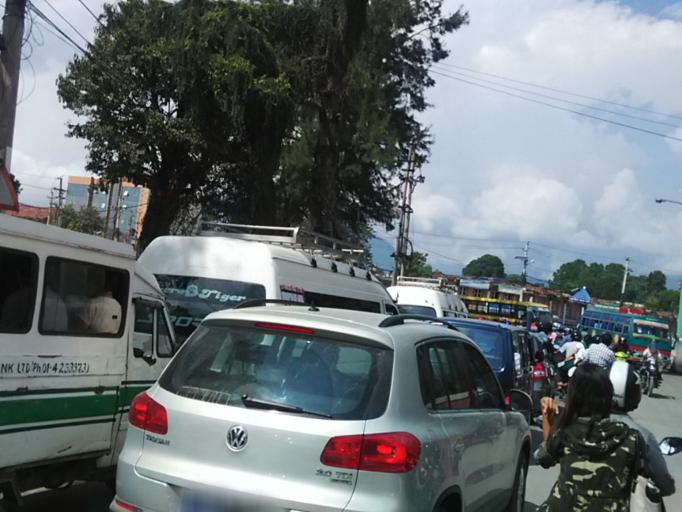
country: NP
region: Central Region
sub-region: Bagmati Zone
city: Kathmandu
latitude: 27.7164
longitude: 85.3159
